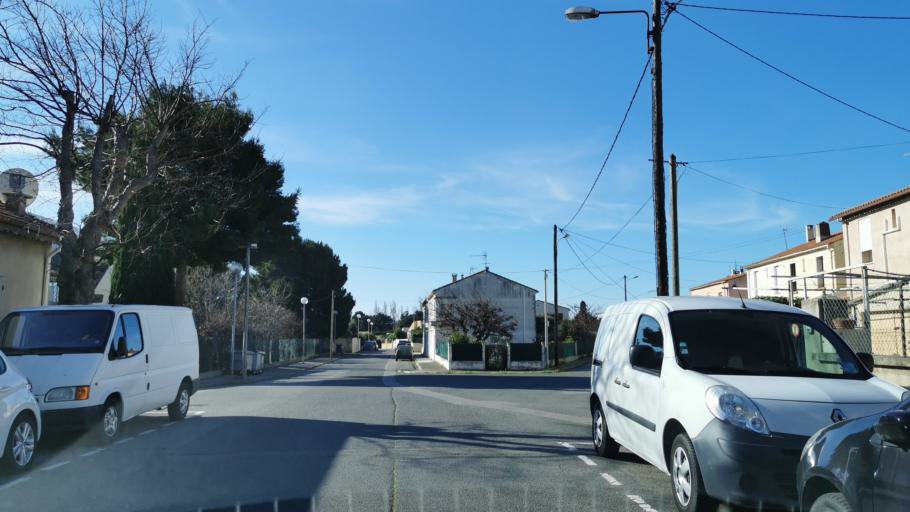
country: FR
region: Languedoc-Roussillon
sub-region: Departement de l'Aude
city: Narbonne
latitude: 43.1775
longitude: 2.9962
